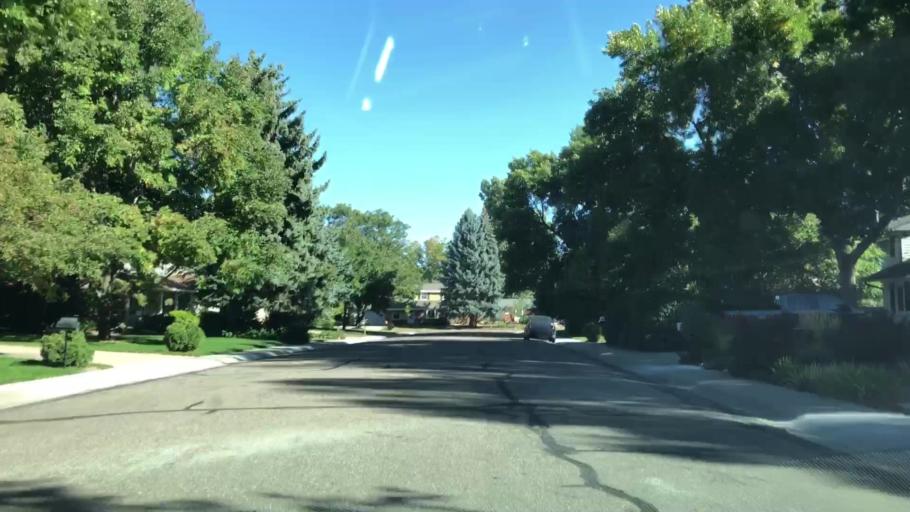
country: US
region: Colorado
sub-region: Larimer County
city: Fort Collins
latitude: 40.5569
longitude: -105.0510
